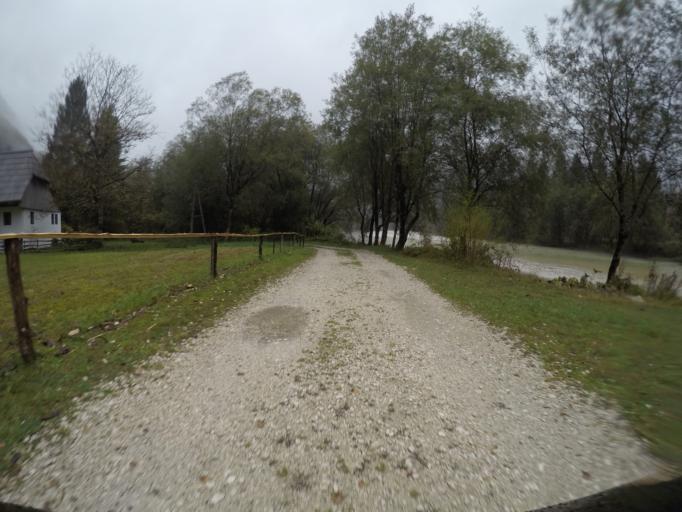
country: SI
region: Bovec
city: Bovec
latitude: 46.3320
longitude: 13.6387
